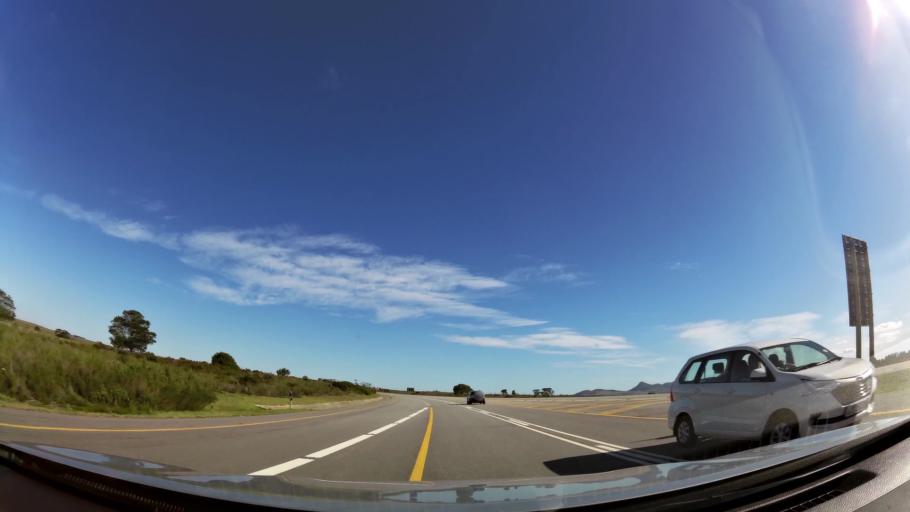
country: ZA
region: Eastern Cape
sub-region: Cacadu District Municipality
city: Kruisfontein
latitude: -34.0306
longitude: 24.5973
